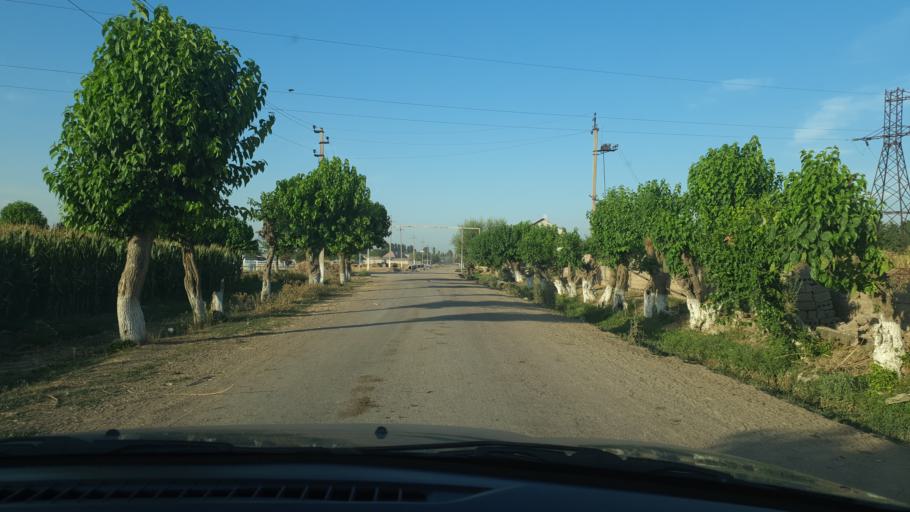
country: UZ
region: Toshkent
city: Tuytepa
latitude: 41.1021
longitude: 69.3850
